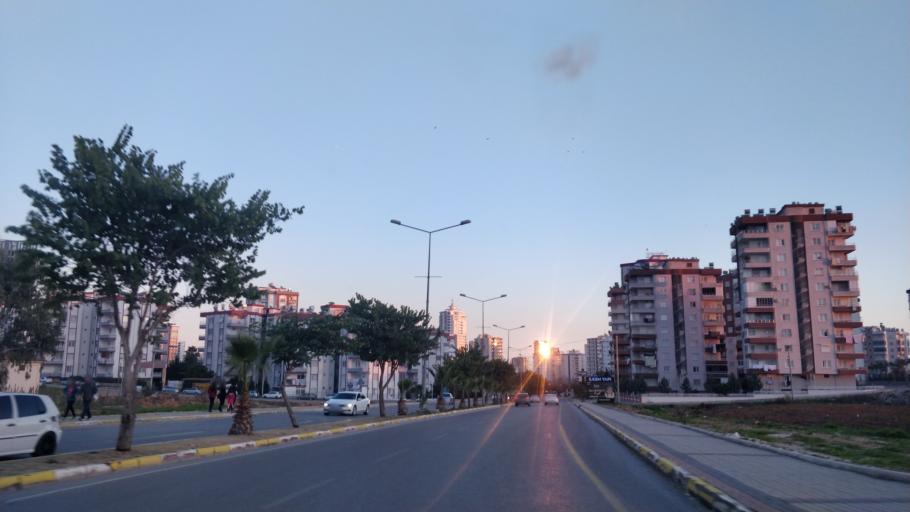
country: TR
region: Mersin
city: Mercin
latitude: 36.7970
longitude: 34.5781
